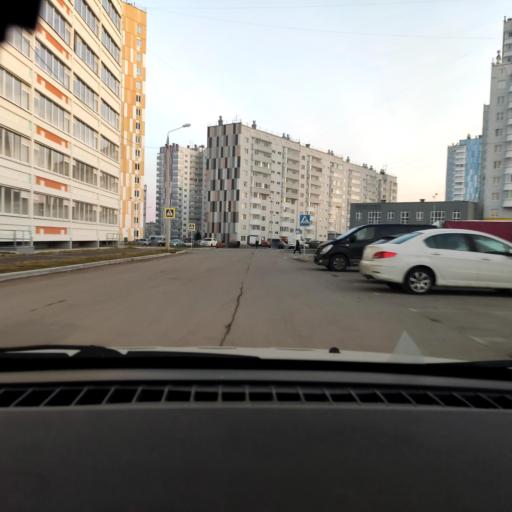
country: RU
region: Perm
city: Perm
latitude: 58.0507
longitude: 56.3511
